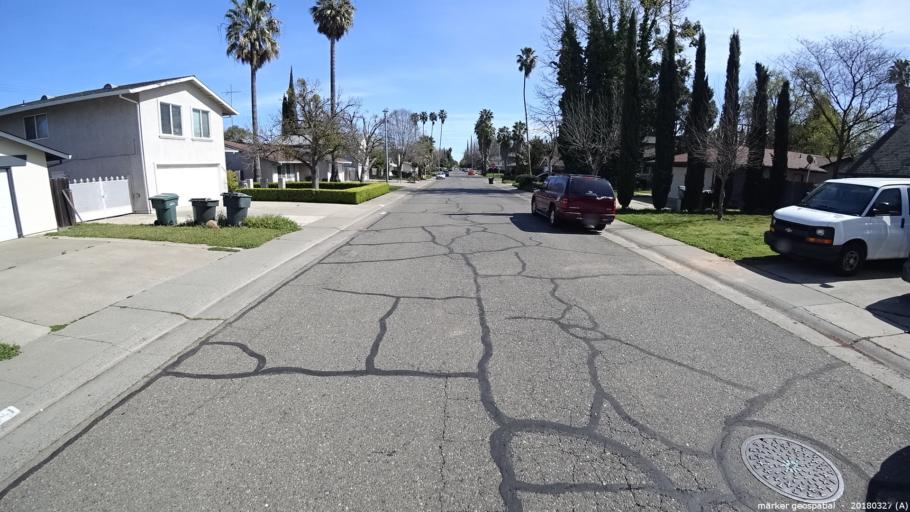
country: US
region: California
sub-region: Sacramento County
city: Rosemont
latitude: 38.5564
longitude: -121.3669
